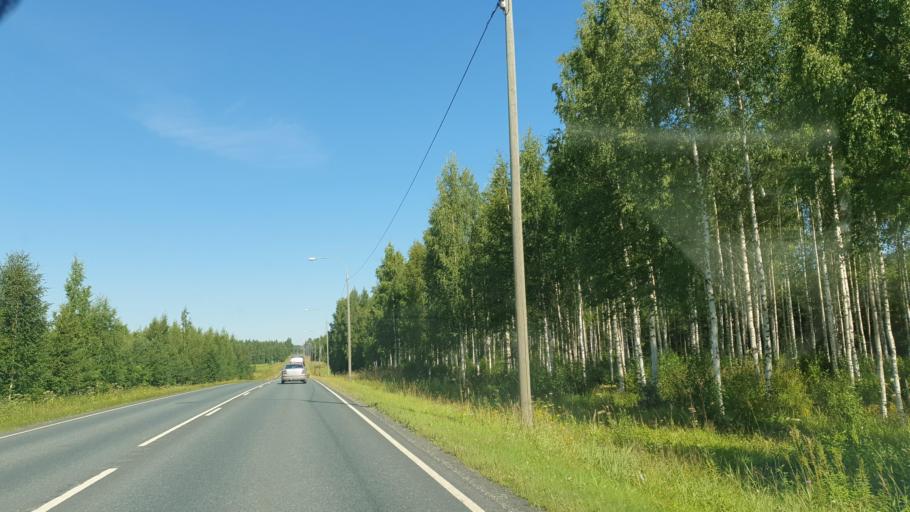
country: FI
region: Northern Savo
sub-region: Ylae-Savo
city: Lapinlahti
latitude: 63.3162
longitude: 27.4456
